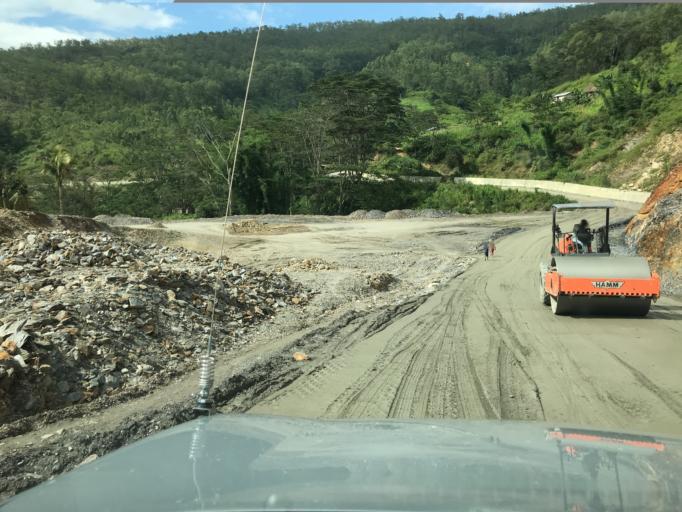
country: TL
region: Aileu
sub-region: Aileu Villa
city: Aileu
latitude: -8.6651
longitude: 125.5500
